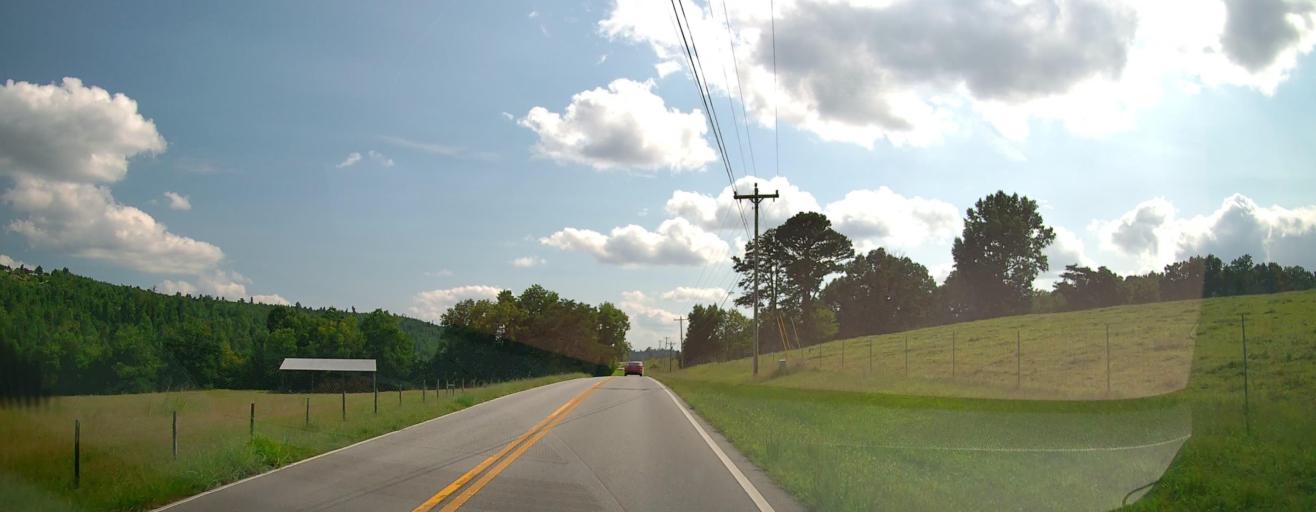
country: US
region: Tennessee
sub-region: Hamilton County
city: Apison
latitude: 34.9768
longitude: -85.0663
